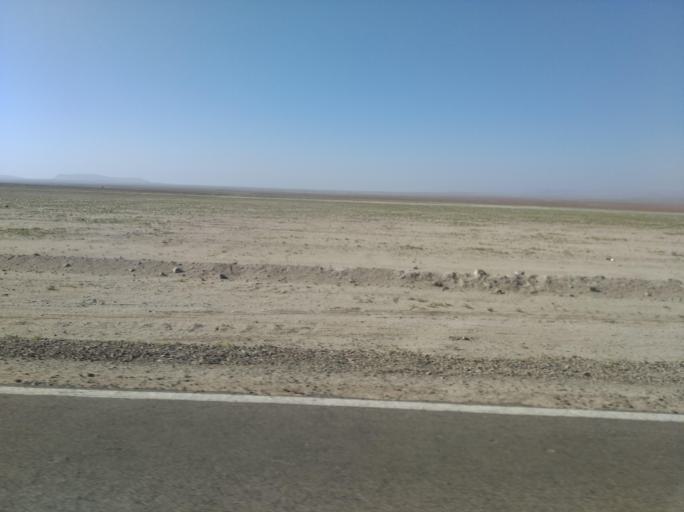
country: CL
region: Atacama
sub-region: Provincia de Copiapo
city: Copiapo
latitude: -27.3162
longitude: -70.8707
